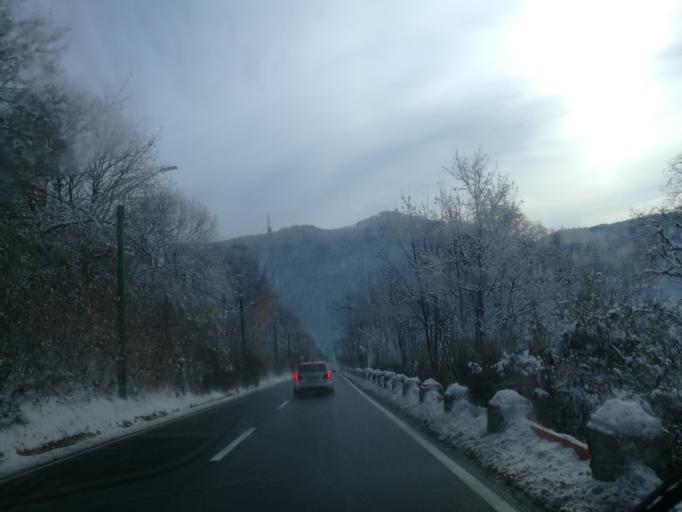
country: RO
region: Brasov
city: Brasov
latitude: 45.6439
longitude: 25.5815
